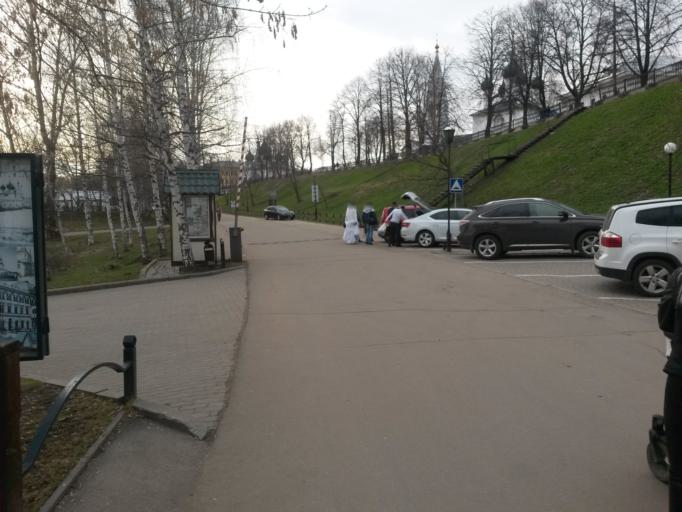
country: RU
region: Jaroslavl
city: Yaroslavl
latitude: 57.6218
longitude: 39.8999
